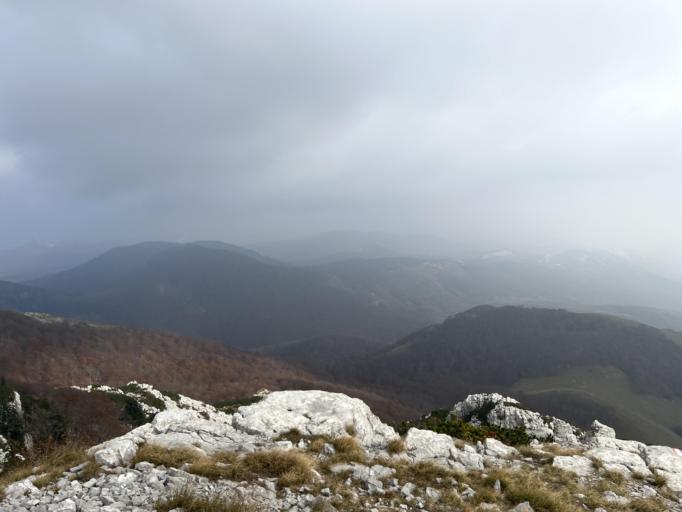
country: HR
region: Primorsko-Goranska
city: Drazice
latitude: 45.4489
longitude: 14.4865
